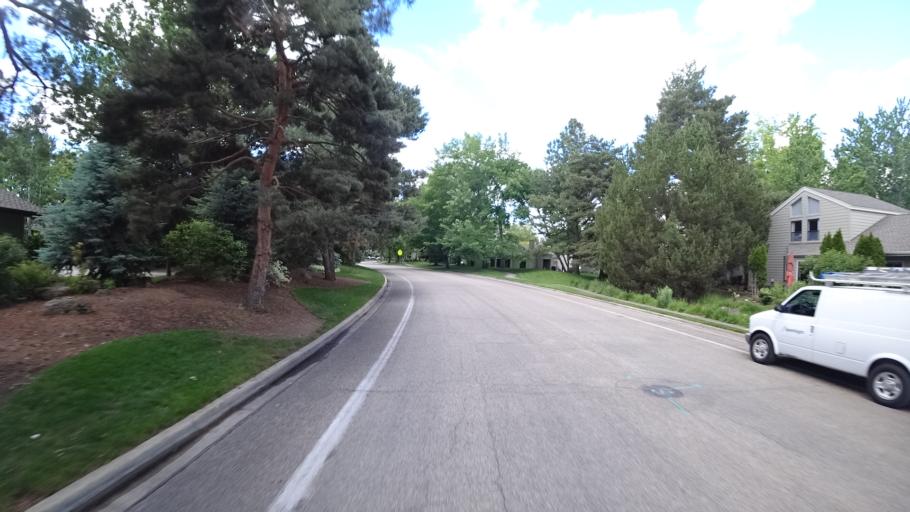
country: US
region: Idaho
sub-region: Ada County
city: Boise
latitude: 43.5880
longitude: -116.1688
